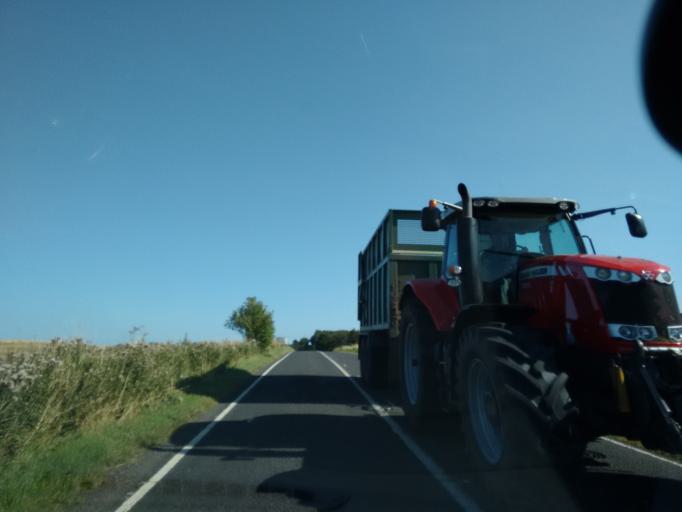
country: GB
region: England
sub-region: Northumberland
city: Acomb
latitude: 55.0175
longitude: -2.0601
